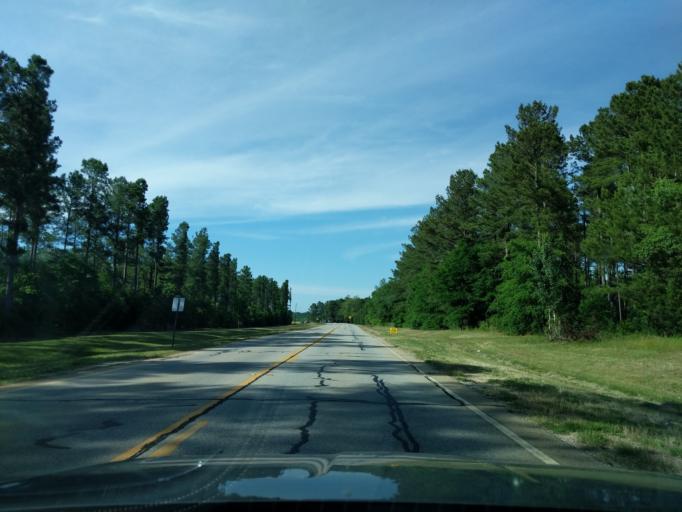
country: US
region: Georgia
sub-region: Jefferson County
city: Wrens
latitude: 33.2589
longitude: -82.3854
